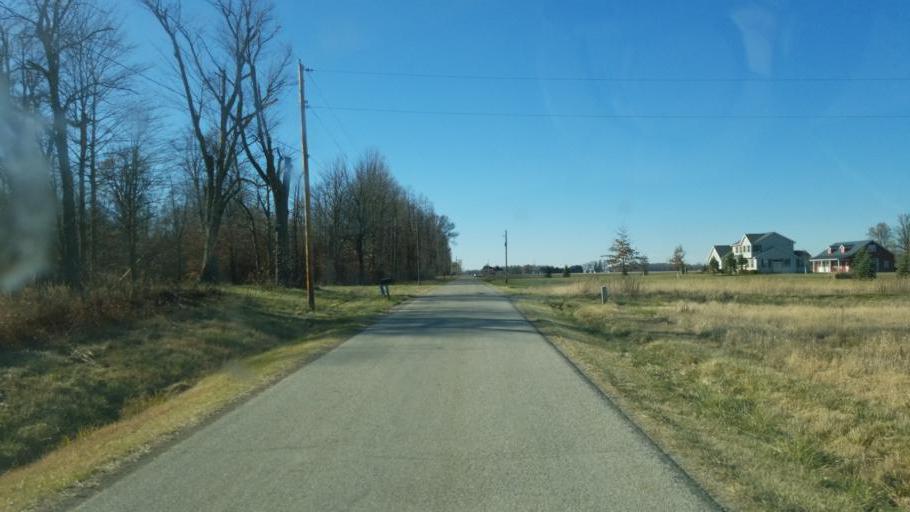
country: US
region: Ohio
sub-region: Crawford County
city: Galion
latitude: 40.7706
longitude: -82.8431
